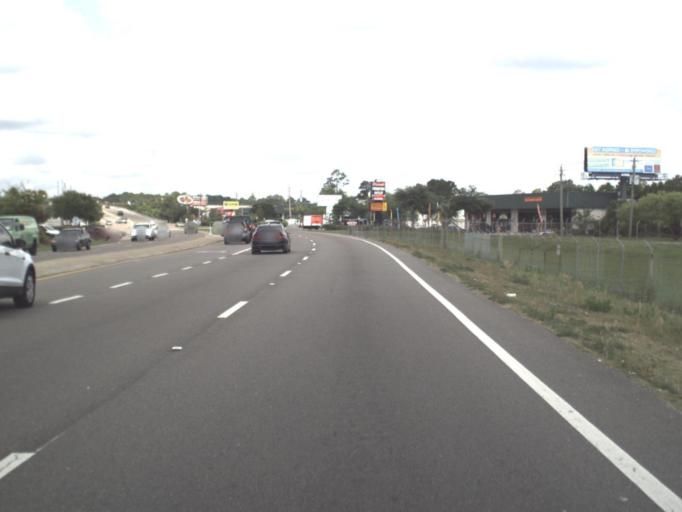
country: US
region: Florida
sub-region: Saint Johns County
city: Saint Augustine South
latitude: 29.8672
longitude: -81.3274
